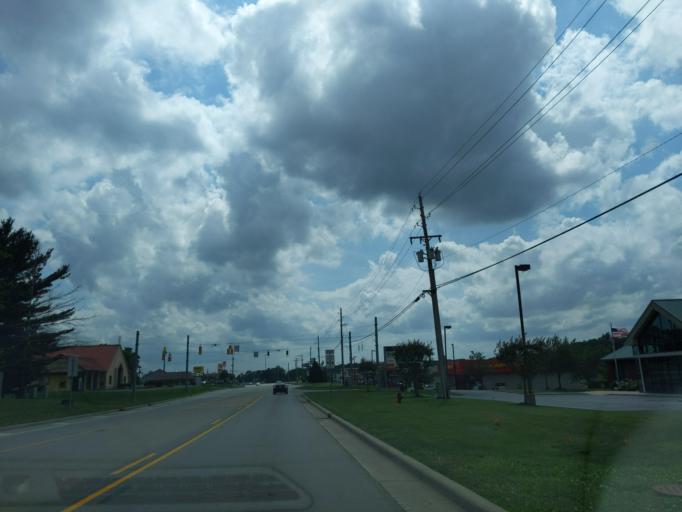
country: US
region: Indiana
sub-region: Ripley County
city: Batesville
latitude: 39.3117
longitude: -85.2121
